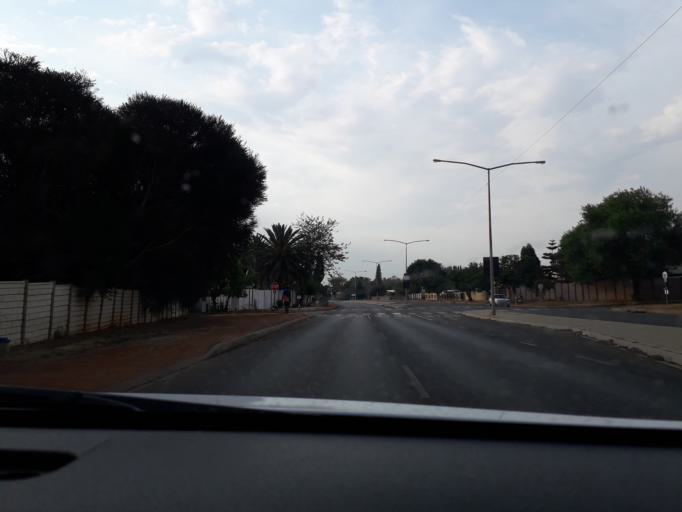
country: ZA
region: Gauteng
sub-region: City of Johannesburg Metropolitan Municipality
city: Modderfontein
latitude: -26.0634
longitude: 28.2065
